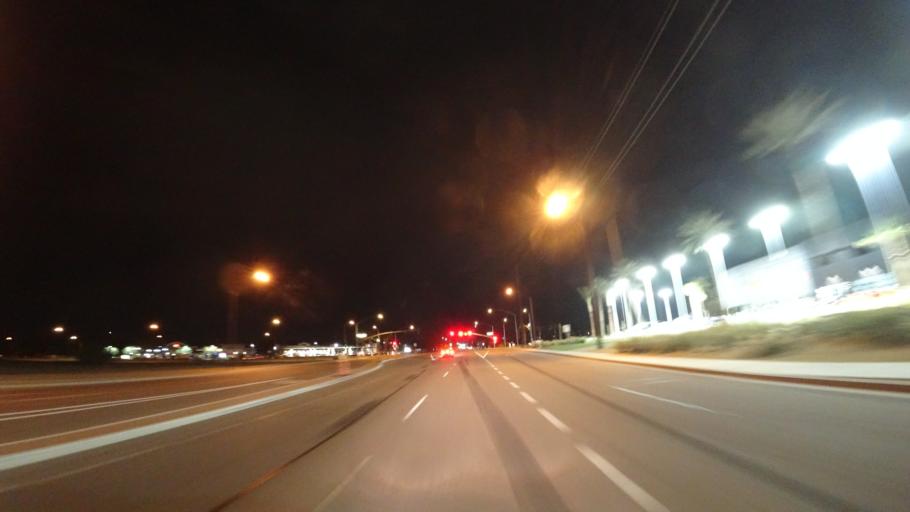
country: US
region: Arizona
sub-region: Maricopa County
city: Chandler
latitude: 33.2918
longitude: -111.7911
